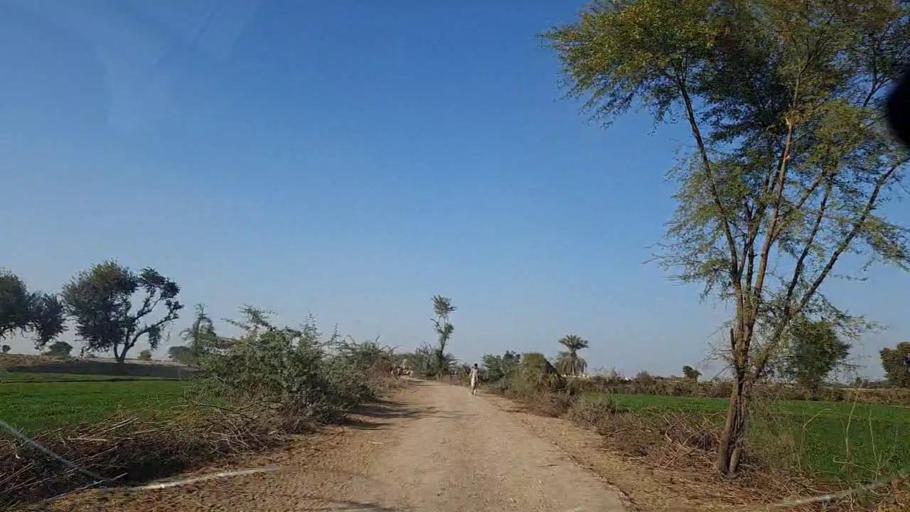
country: PK
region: Sindh
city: Khanpur
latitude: 27.7714
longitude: 69.2902
